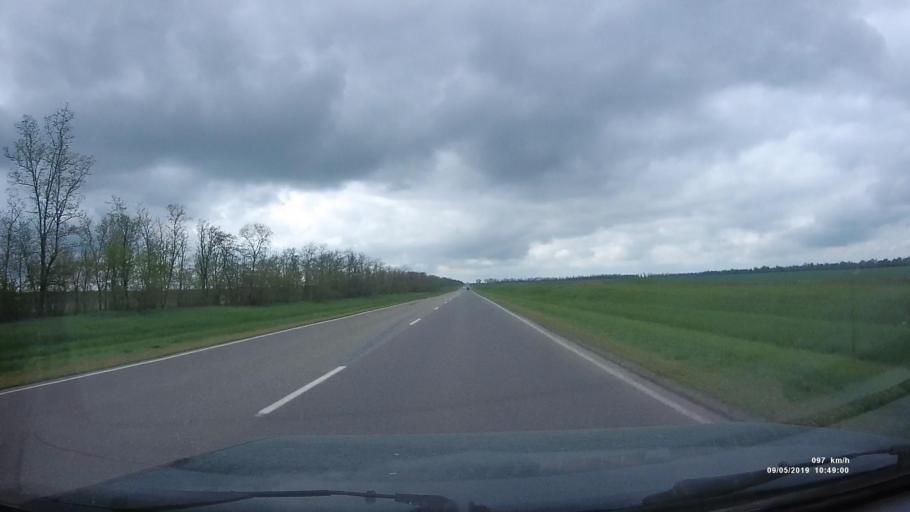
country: RU
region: Rostov
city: Peshkovo
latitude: 46.9485
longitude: 39.3555
